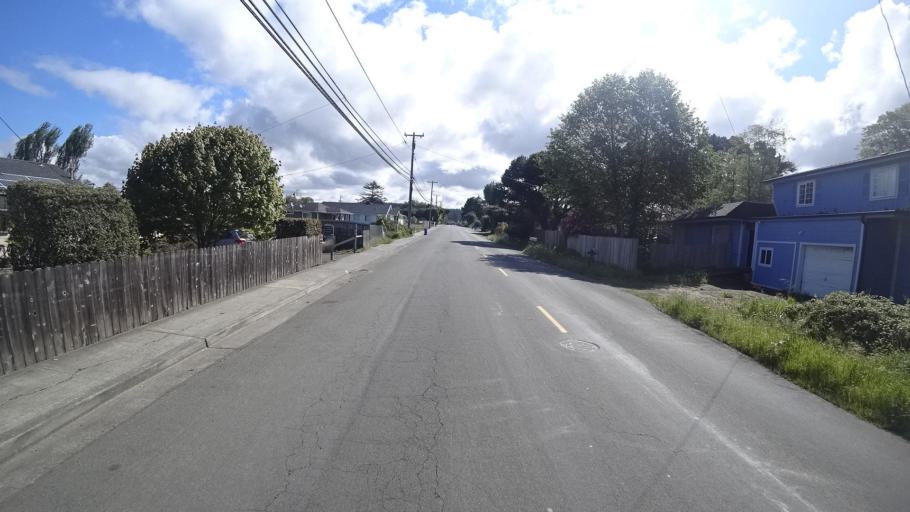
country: US
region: California
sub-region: Humboldt County
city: McKinleyville
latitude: 40.9455
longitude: -124.1056
